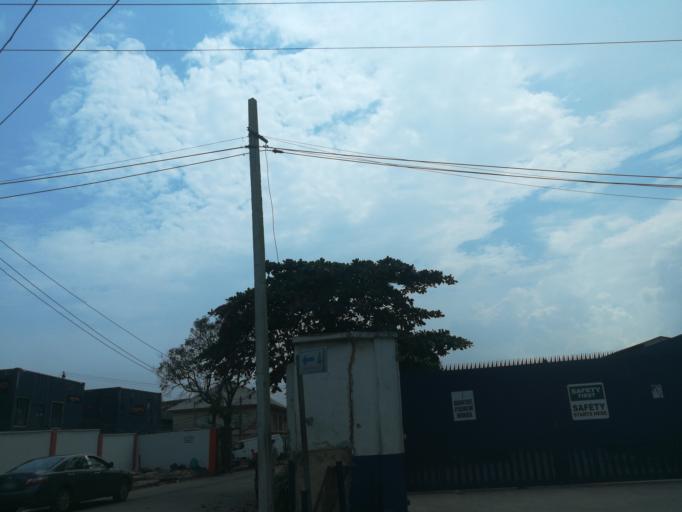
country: NG
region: Lagos
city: Ikeja
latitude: 6.6056
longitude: 3.3656
